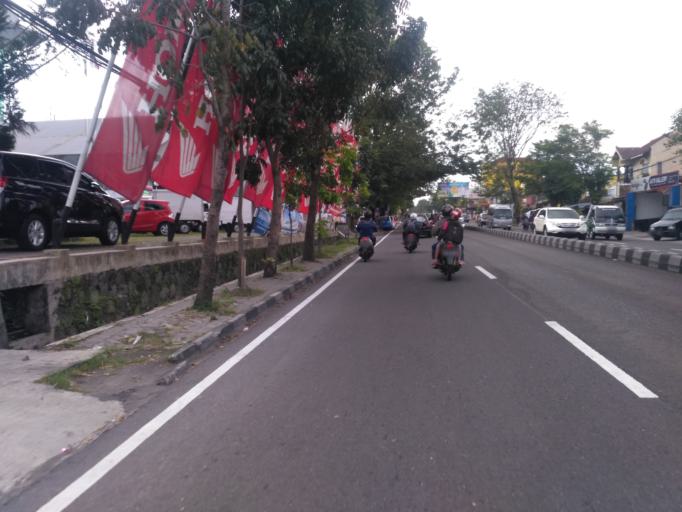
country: ID
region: Daerah Istimewa Yogyakarta
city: Melati
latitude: -7.7425
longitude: 110.3626
